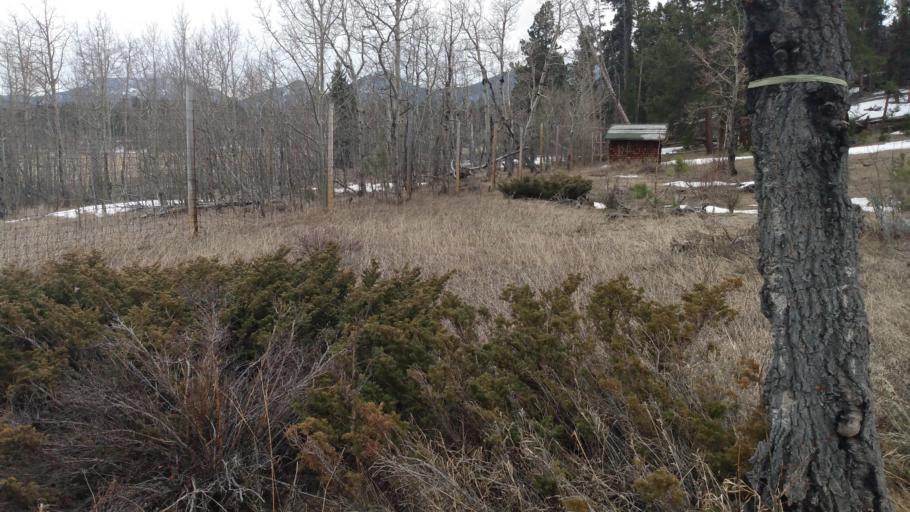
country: US
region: Colorado
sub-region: Larimer County
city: Estes Park
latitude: 40.3727
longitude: -105.6157
